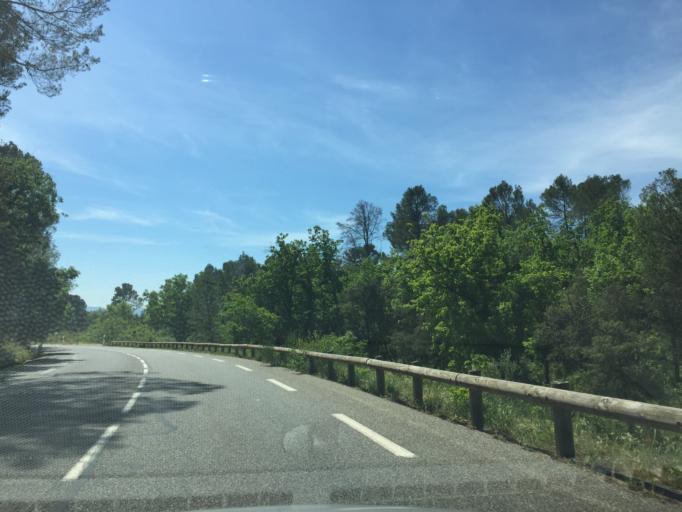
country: FR
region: Provence-Alpes-Cote d'Azur
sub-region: Departement du Var
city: Lorgues
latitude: 43.5068
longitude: 6.3390
